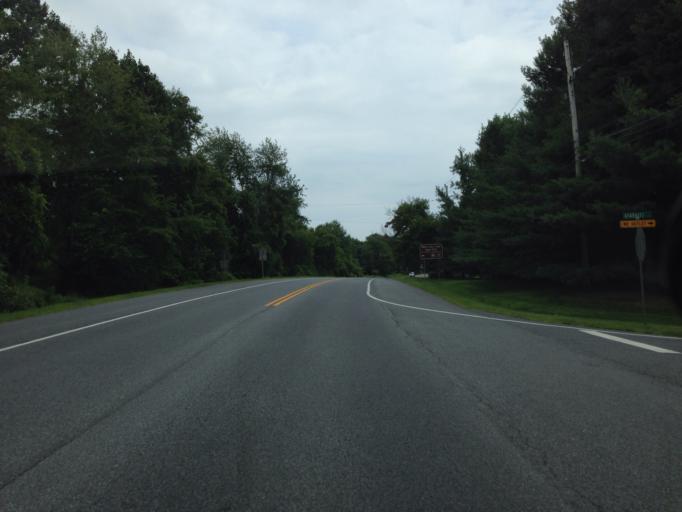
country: US
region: Delaware
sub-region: New Castle County
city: Newark
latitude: 39.7165
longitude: -75.7831
